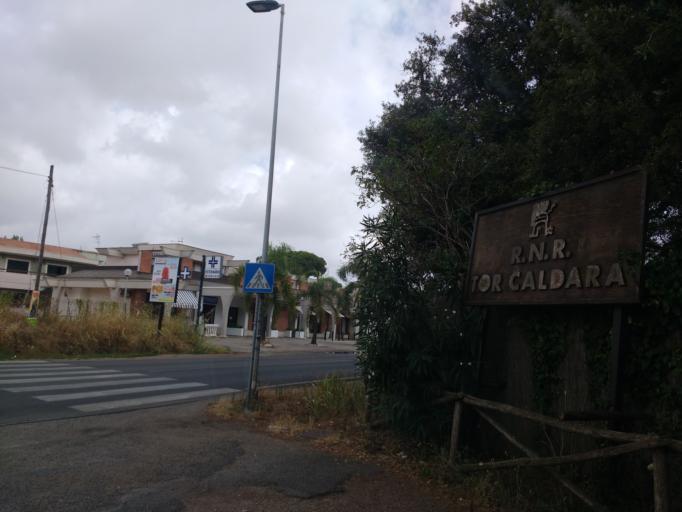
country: IT
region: Latium
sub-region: Citta metropolitana di Roma Capitale
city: Lavinio
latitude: 41.4906
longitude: 12.5962
